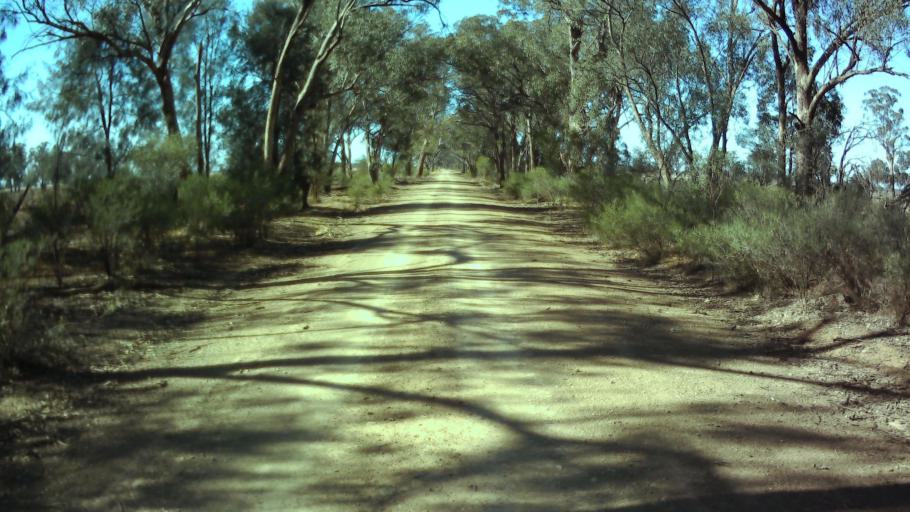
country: AU
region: New South Wales
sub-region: Weddin
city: Grenfell
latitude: -33.9406
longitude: 147.8710
